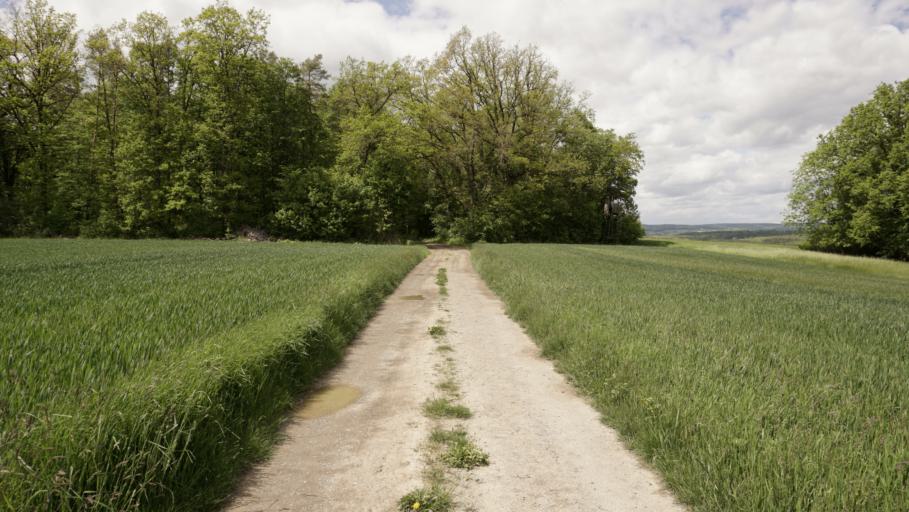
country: DE
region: Baden-Wuerttemberg
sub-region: Karlsruhe Region
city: Mosbach
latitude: 49.3689
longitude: 9.1707
